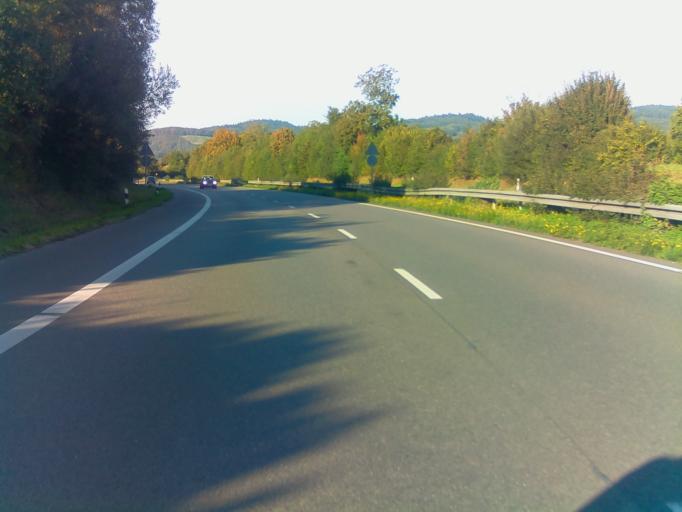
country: DE
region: Baden-Wuerttemberg
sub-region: Karlsruhe Region
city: Weinheim
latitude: 49.5514
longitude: 8.6396
